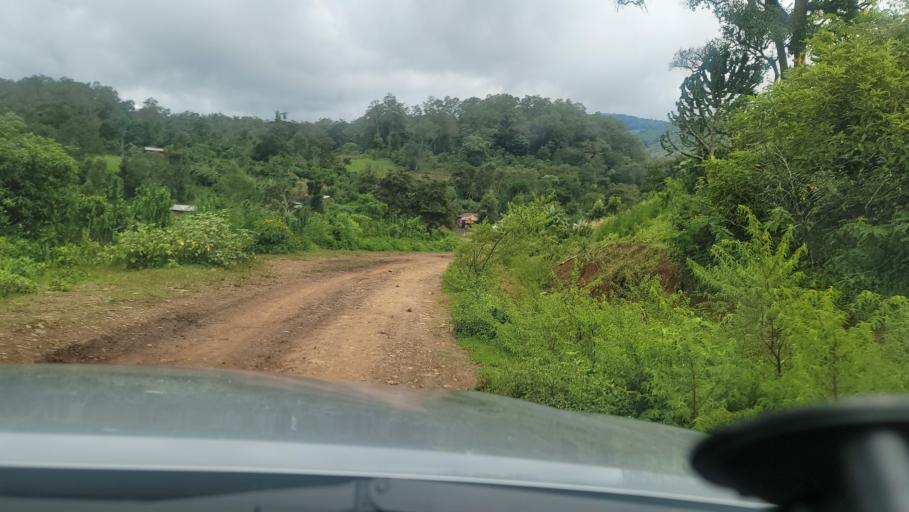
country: ET
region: Southern Nations, Nationalities, and People's Region
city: Bonga
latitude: 7.6336
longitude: 36.2232
